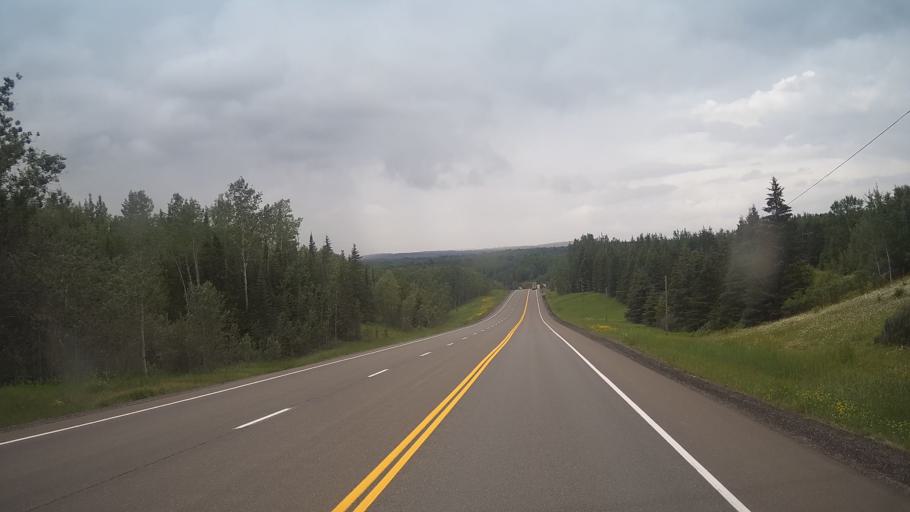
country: CA
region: Ontario
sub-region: Thunder Bay District
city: Thunder Bay
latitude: 48.5316
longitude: -89.5489
